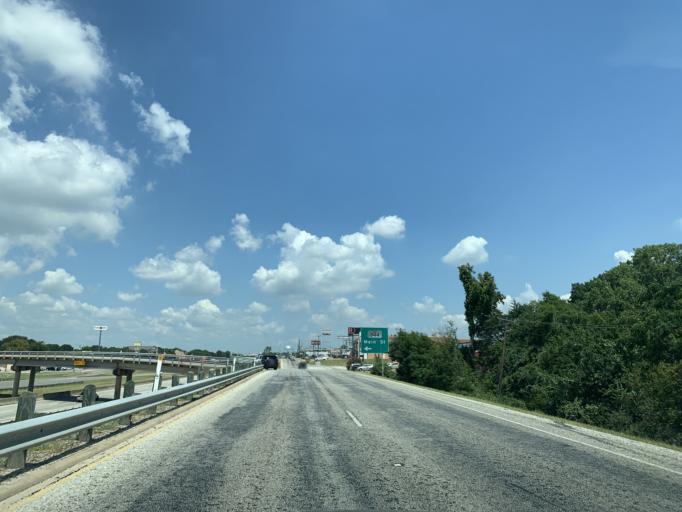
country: US
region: Texas
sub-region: Tarrant County
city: Azle
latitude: 32.8891
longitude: -97.5391
